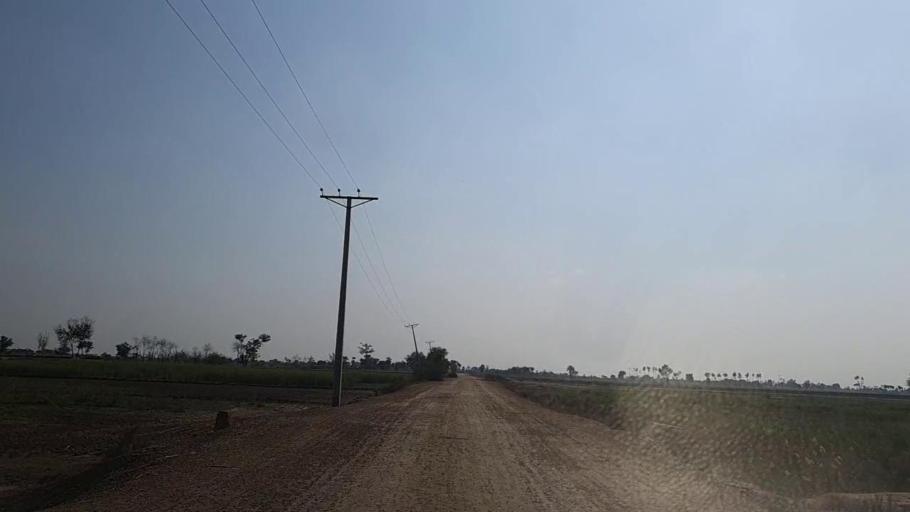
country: PK
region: Sindh
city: Daur
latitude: 26.4606
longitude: 68.2349
